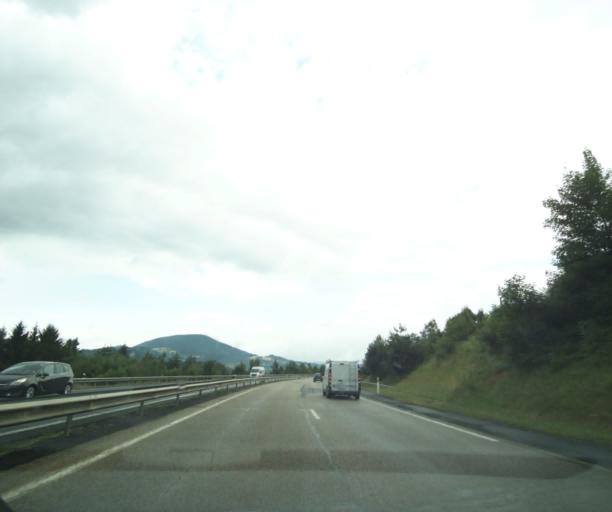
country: FR
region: Auvergne
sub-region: Departement de la Haute-Loire
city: Yssingeaux
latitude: 45.1151
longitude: 4.0758
